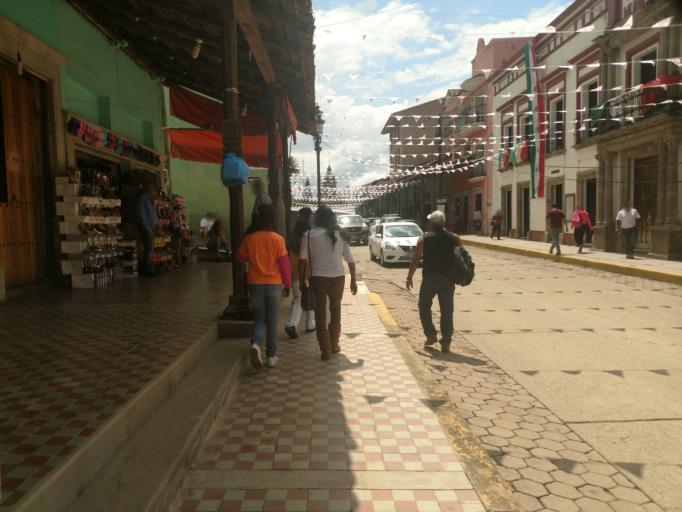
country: MX
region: Jalisco
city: Talpa de Allende
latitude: 20.3824
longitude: -104.8232
